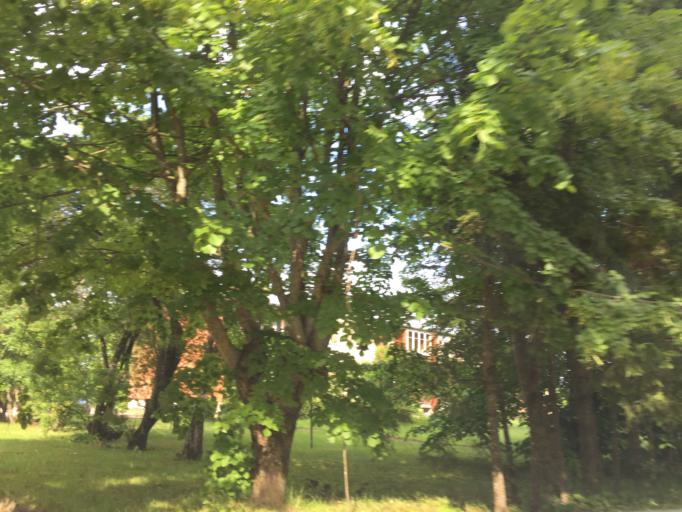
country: LV
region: Pargaujas
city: Stalbe
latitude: 57.3458
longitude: 24.9477
